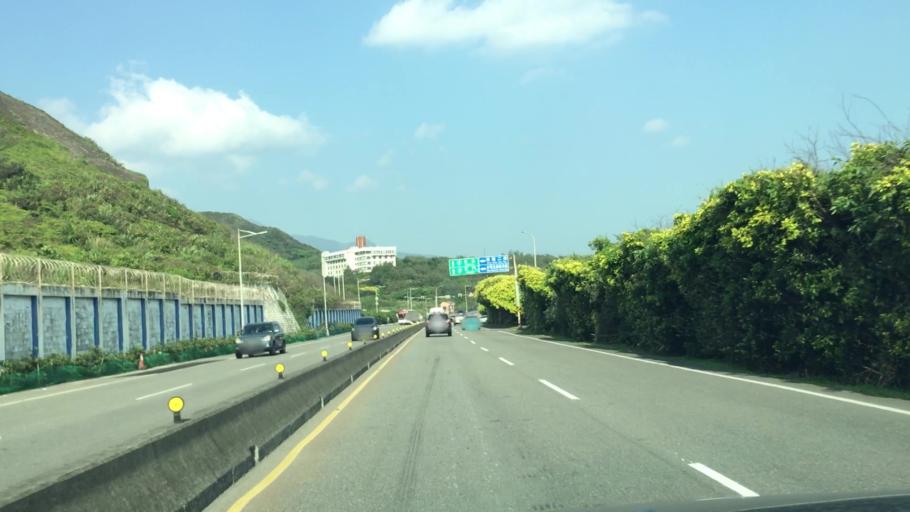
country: TW
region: Taiwan
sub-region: Keelung
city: Keelung
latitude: 25.2064
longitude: 121.6621
